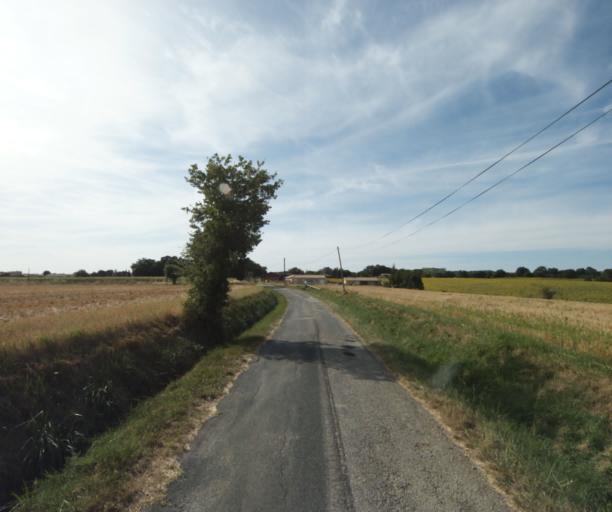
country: FR
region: Midi-Pyrenees
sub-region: Departement du Tarn
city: Soual
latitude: 43.5333
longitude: 2.0684
